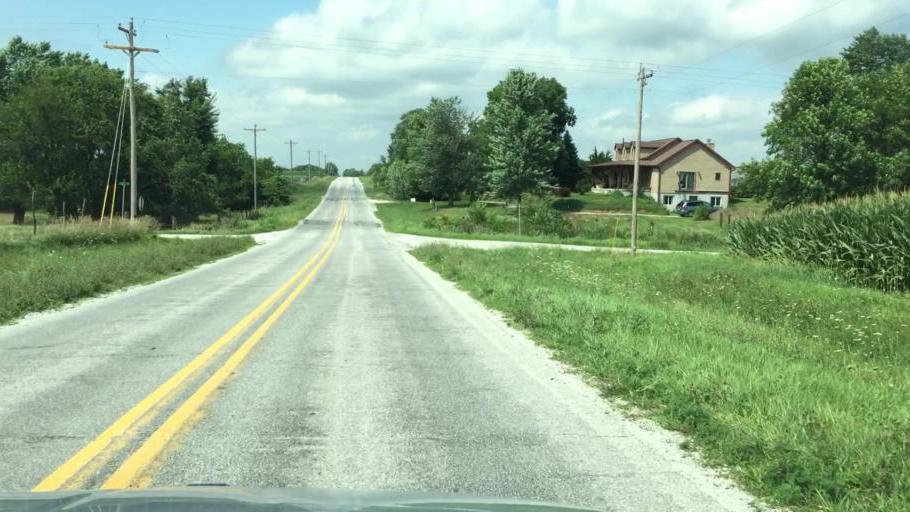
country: US
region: Illinois
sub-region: Hancock County
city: Nauvoo
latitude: 40.5215
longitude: -91.3077
